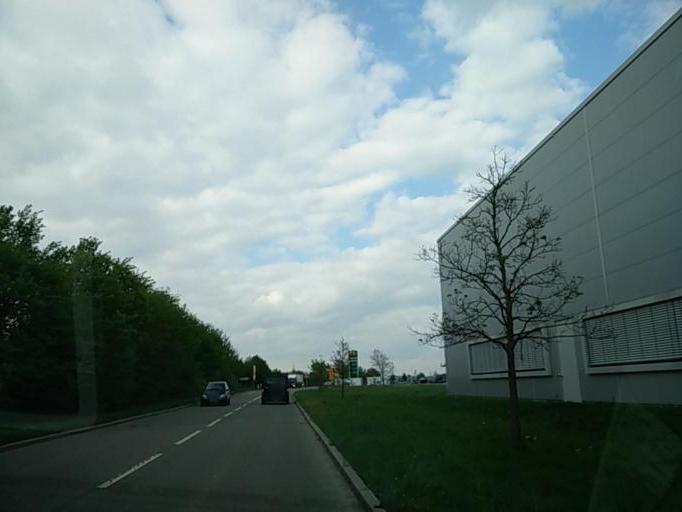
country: DE
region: Baden-Wuerttemberg
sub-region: Tuebingen Region
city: Mossingen
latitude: 48.4174
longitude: 9.0534
